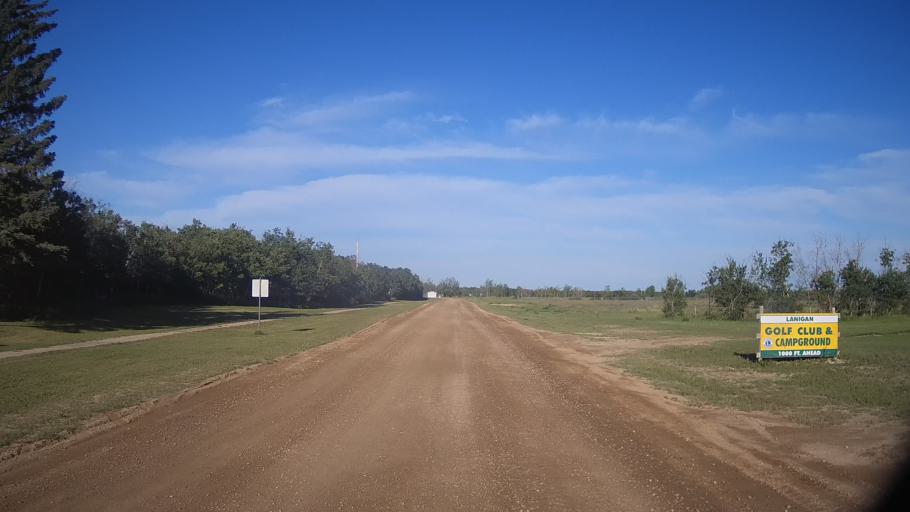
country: CA
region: Saskatchewan
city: Lanigan
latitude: 51.8508
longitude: -105.0235
